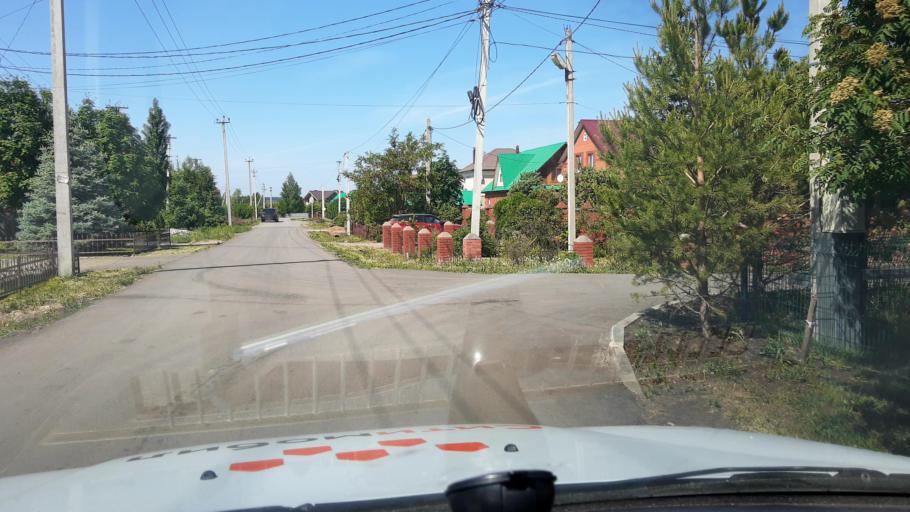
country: RU
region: Bashkortostan
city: Avdon
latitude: 54.4921
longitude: 55.8695
